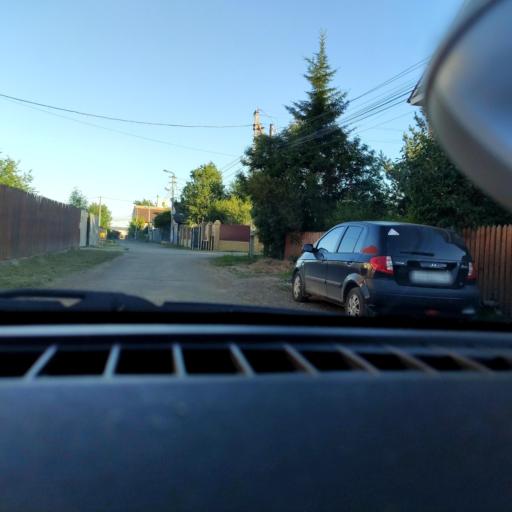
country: RU
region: Perm
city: Froly
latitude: 57.8879
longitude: 56.2546
